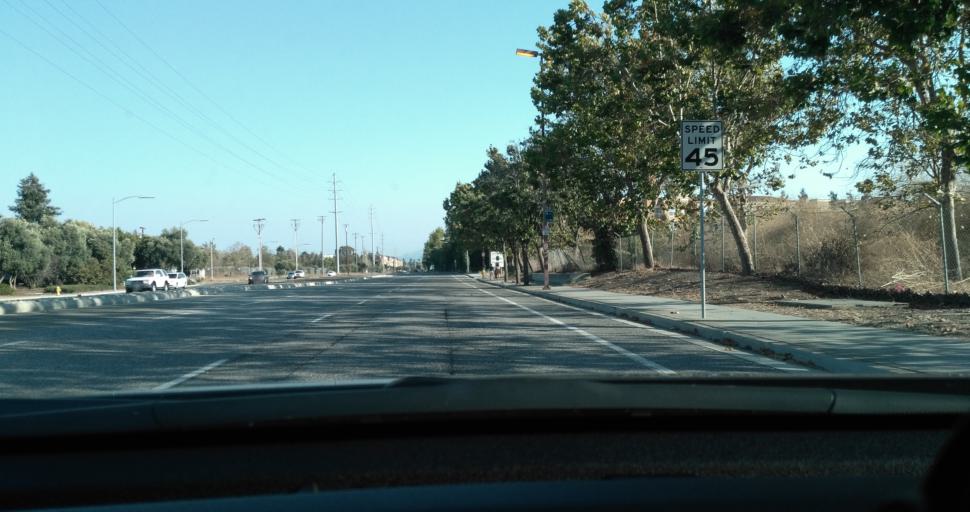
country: US
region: California
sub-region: Santa Clara County
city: Milpitas
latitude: 37.4120
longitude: -121.9372
